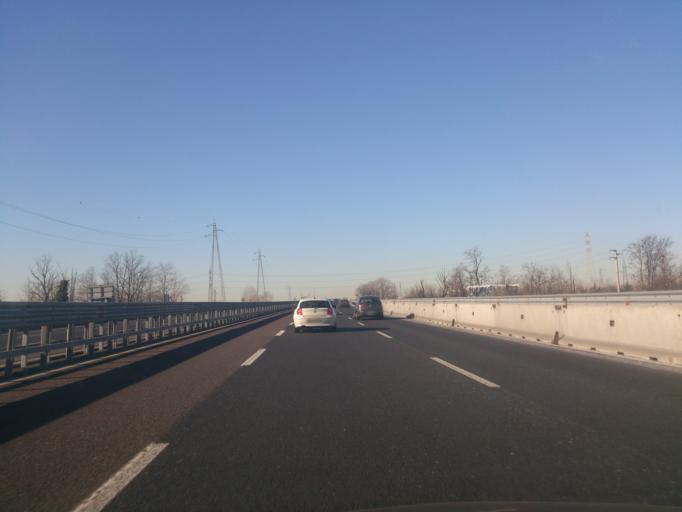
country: IT
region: Lombardy
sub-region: Citta metropolitana di Milano
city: Poasco-Sorigherio
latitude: 45.3843
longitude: 9.2382
